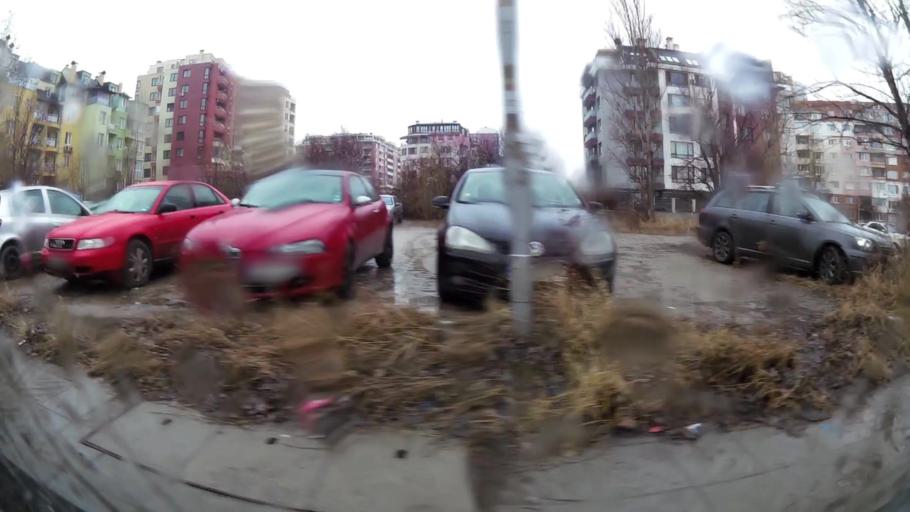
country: BG
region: Sofia-Capital
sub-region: Stolichna Obshtina
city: Sofia
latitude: 42.6643
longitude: 23.3832
